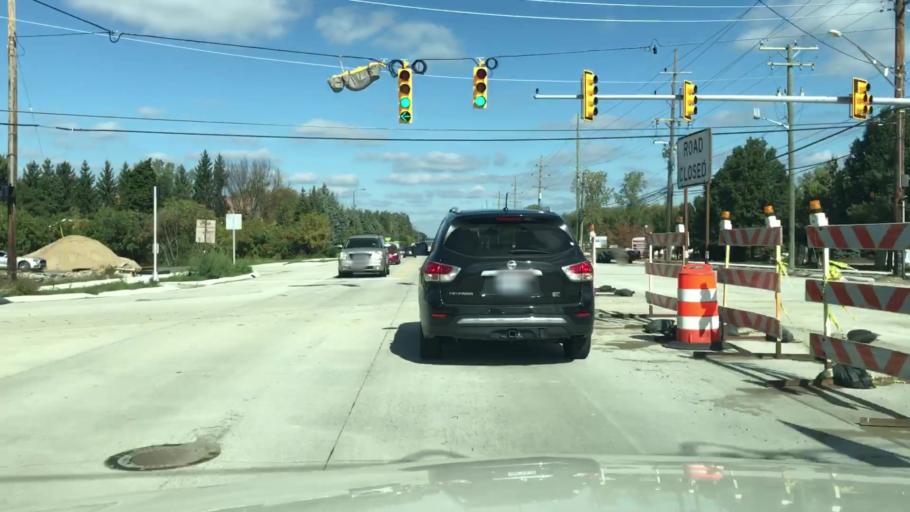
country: US
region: Michigan
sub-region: Oakland County
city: Troy
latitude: 42.6074
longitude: -83.0907
